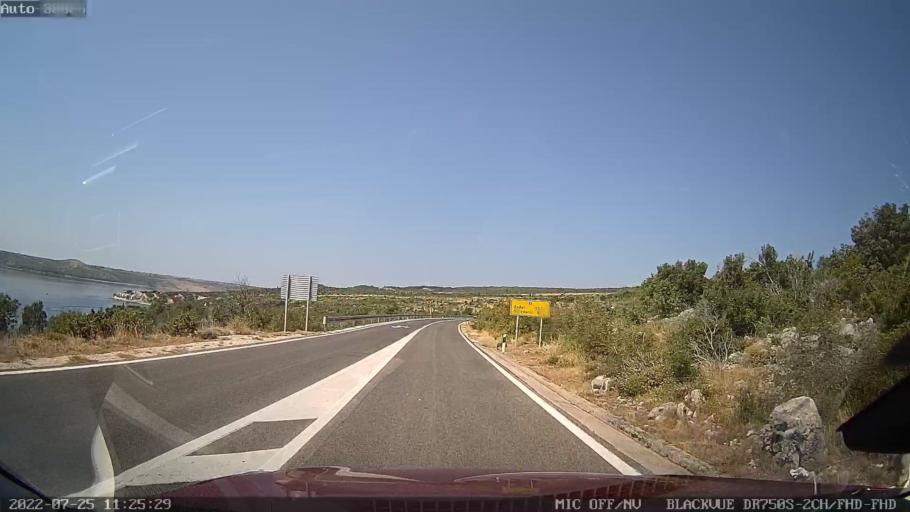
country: HR
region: Zadarska
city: Posedarje
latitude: 44.2224
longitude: 15.5210
